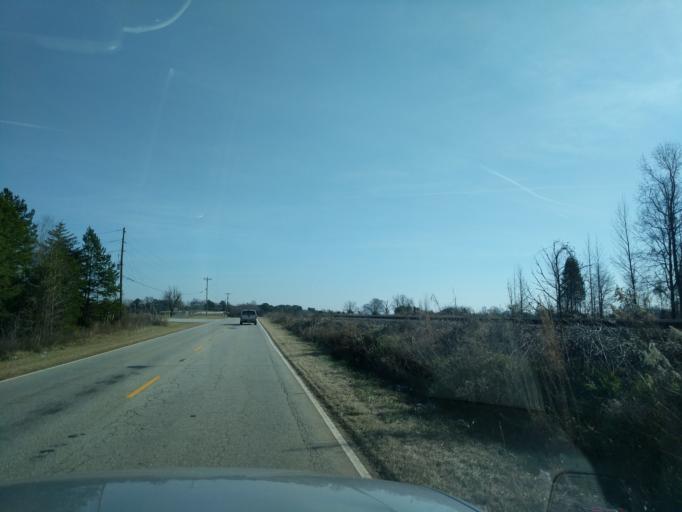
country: US
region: South Carolina
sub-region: Spartanburg County
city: Woodruff
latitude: 34.6978
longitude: -82.0033
